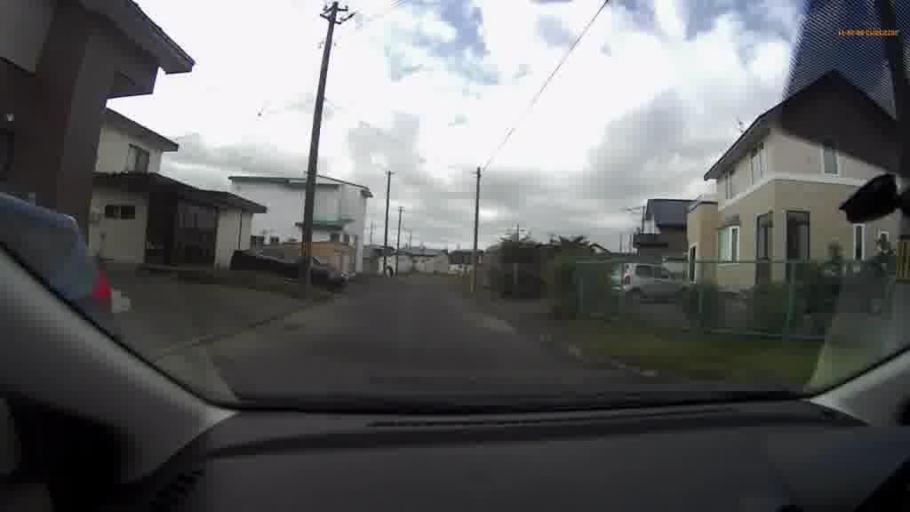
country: JP
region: Hokkaido
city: Kushiro
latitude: 42.9754
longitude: 144.1284
